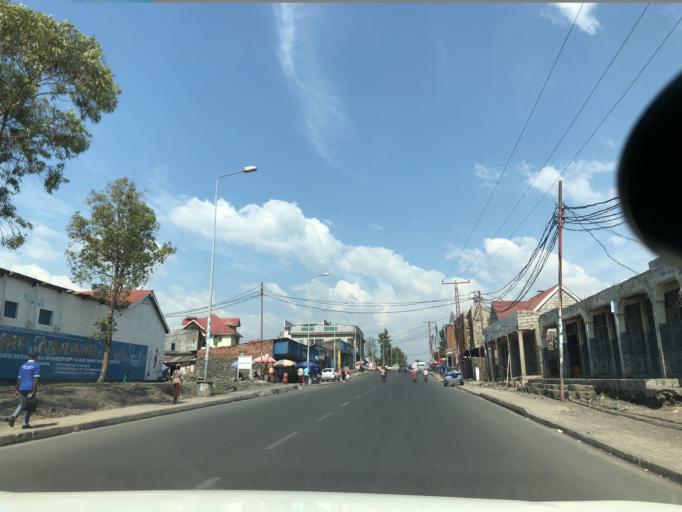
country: CD
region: Nord Kivu
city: Goma
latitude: -1.6588
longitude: 29.1893
